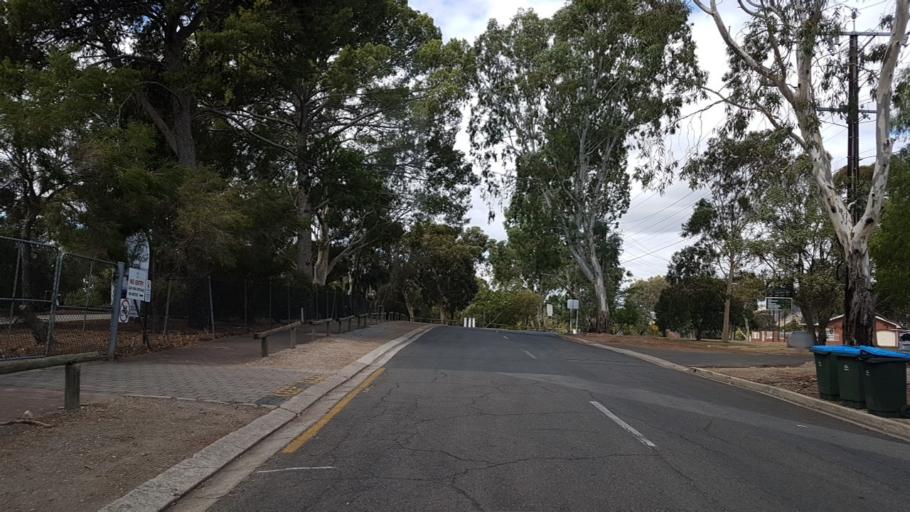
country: AU
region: South Australia
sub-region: Campbelltown
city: Athelstone
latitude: -34.8758
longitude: 138.6900
